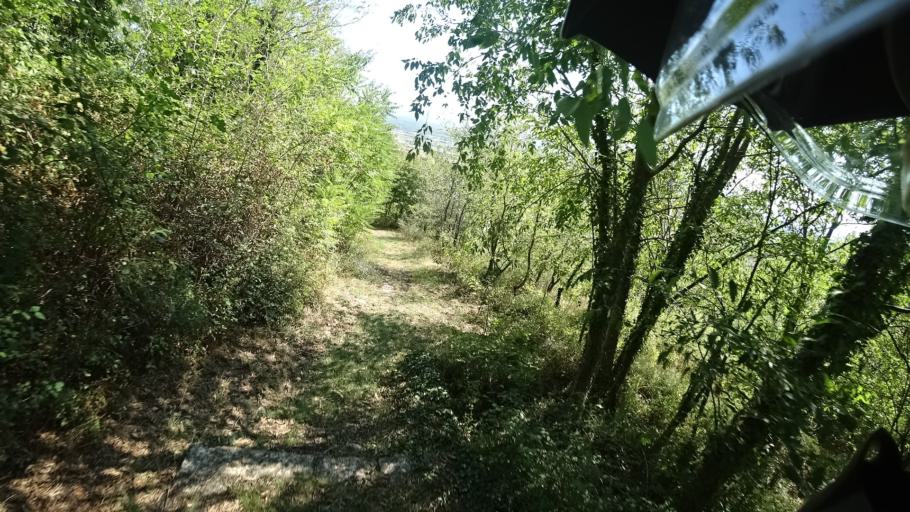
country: HR
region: Sibensko-Kniniska
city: Drnis
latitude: 43.8776
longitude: 16.1970
